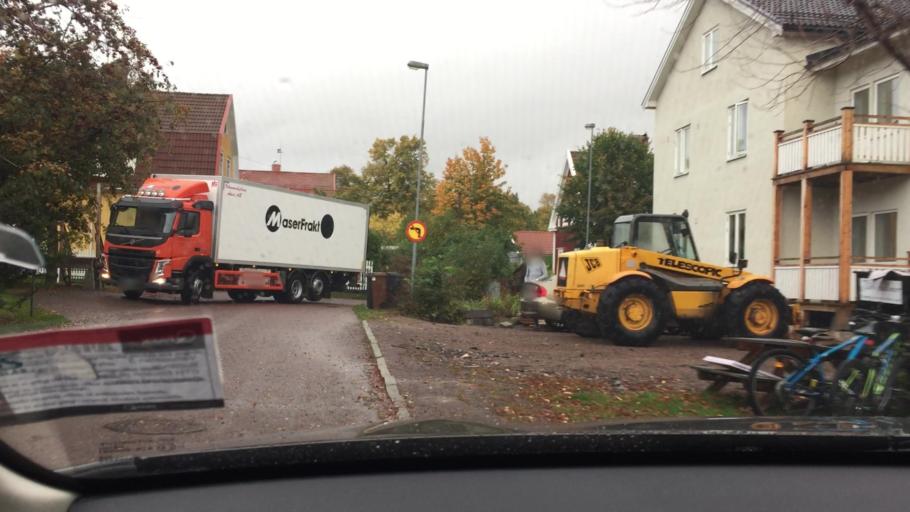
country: SE
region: Dalarna
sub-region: Borlange Kommun
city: Borlaenge
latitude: 60.4824
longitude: 15.4408
